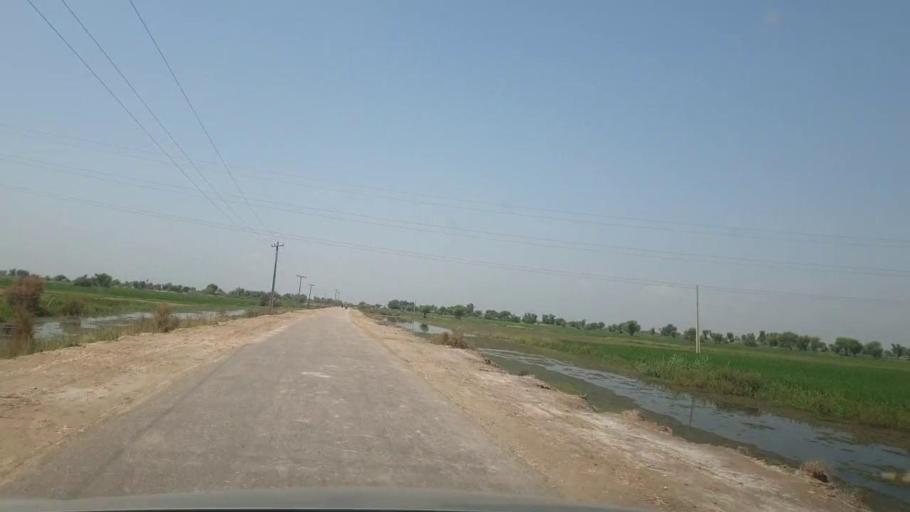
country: PK
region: Sindh
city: Warah
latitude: 27.4835
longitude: 67.7437
